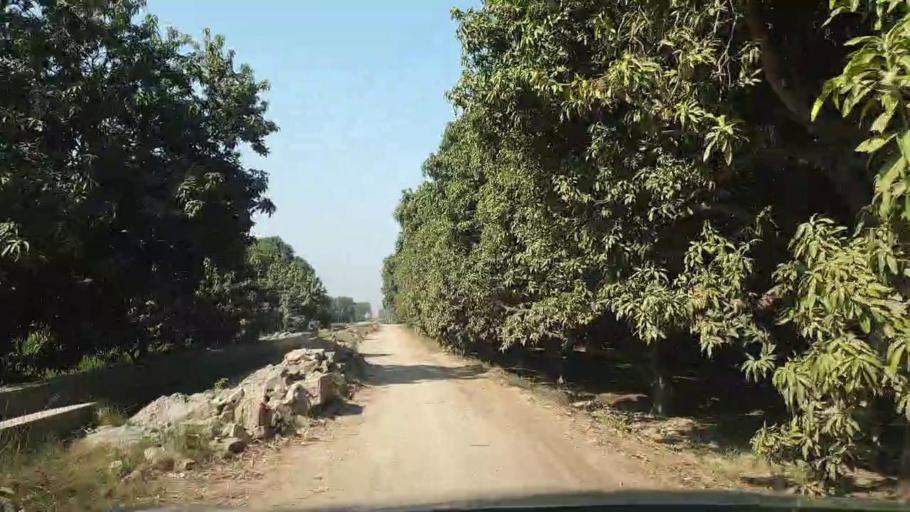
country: PK
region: Sindh
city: Tando Allahyar
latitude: 25.5152
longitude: 68.6994
